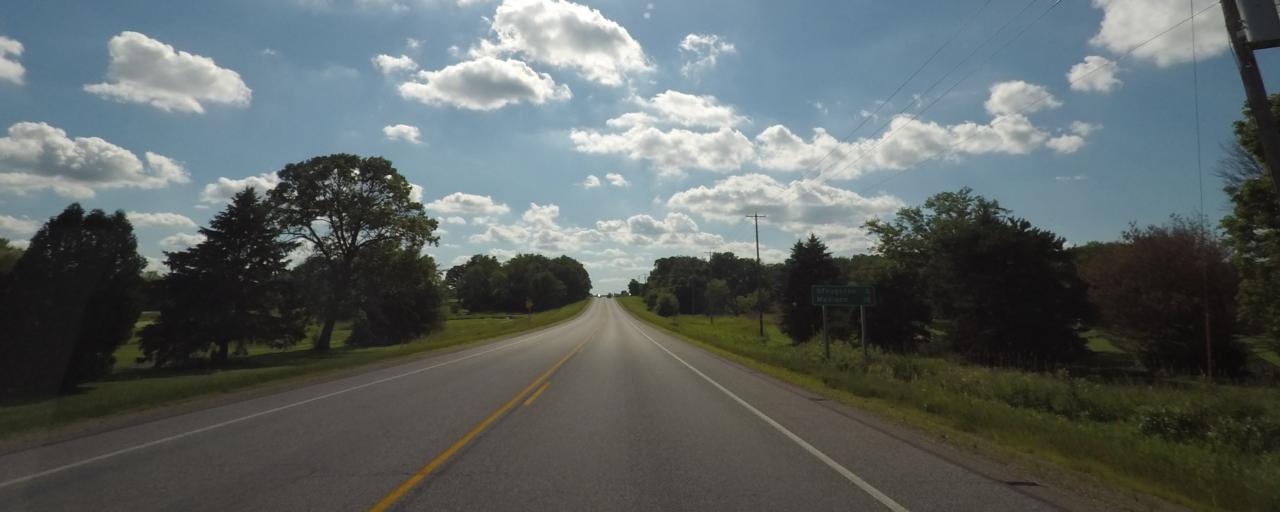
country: US
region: Wisconsin
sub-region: Rock County
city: Edgerton
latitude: 42.9203
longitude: -89.1018
